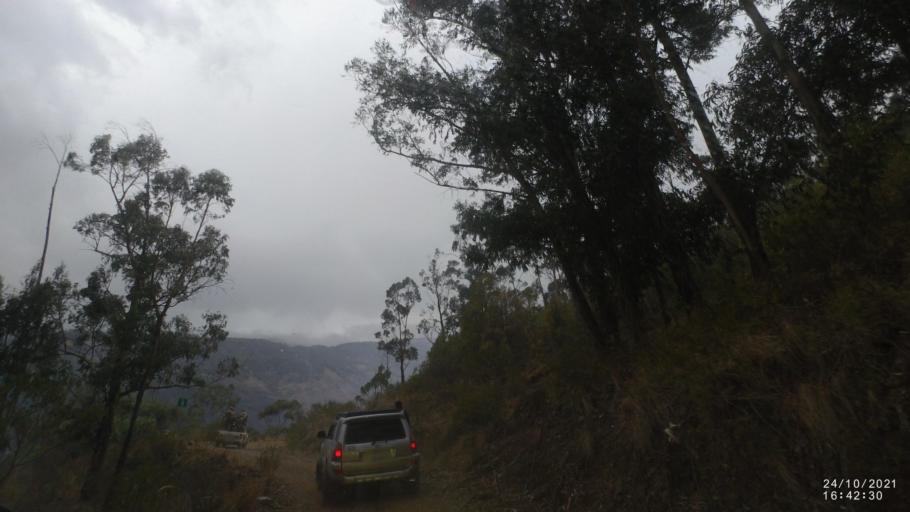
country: BO
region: Cochabamba
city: Cochabamba
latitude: -17.3399
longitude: -66.1472
